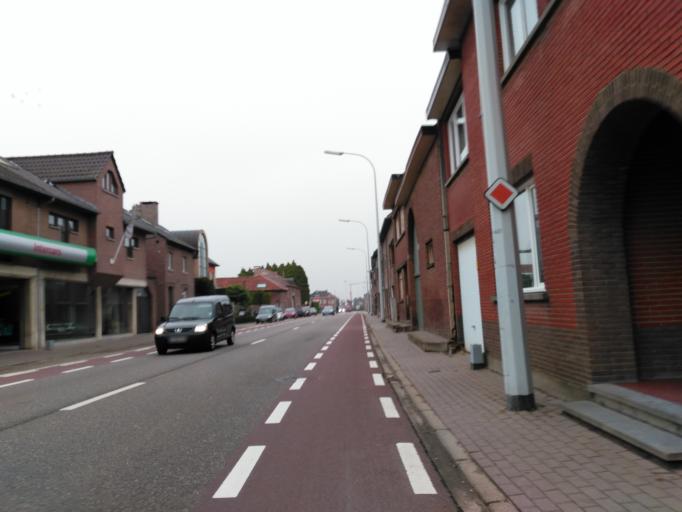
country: BE
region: Flanders
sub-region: Provincie Limburg
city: Lanaken
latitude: 50.8602
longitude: 5.6285
